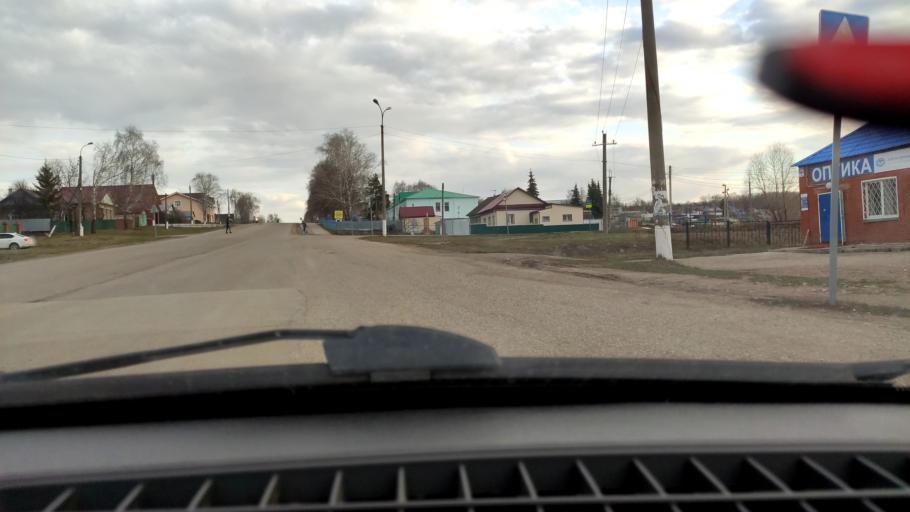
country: RU
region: Bashkortostan
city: Tolbazy
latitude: 54.0219
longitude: 55.8863
